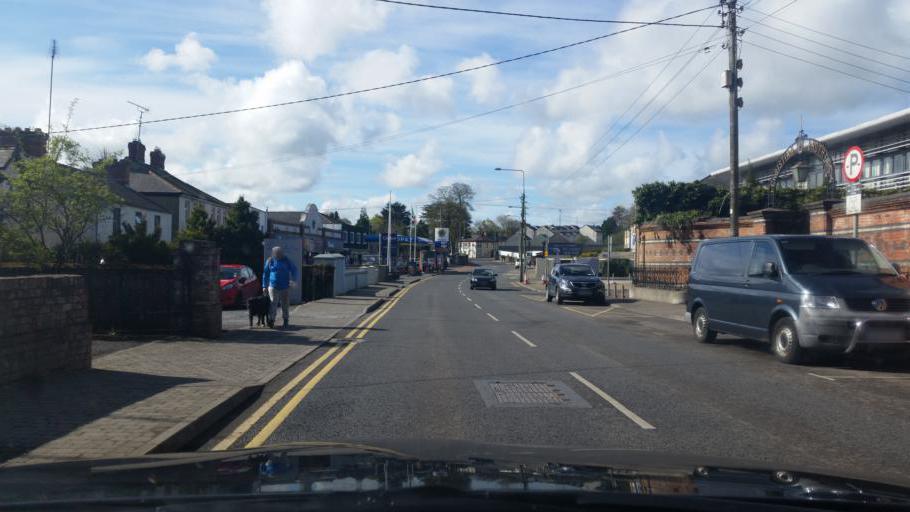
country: IE
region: Leinster
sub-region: An Mhi
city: Kells
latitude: 53.7238
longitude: -6.8806
